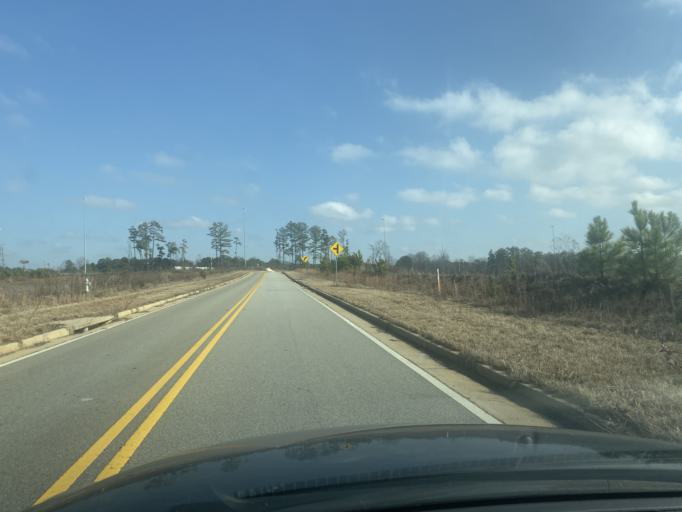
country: US
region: Georgia
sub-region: Henry County
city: Stockbridge
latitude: 33.4800
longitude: -84.2205
